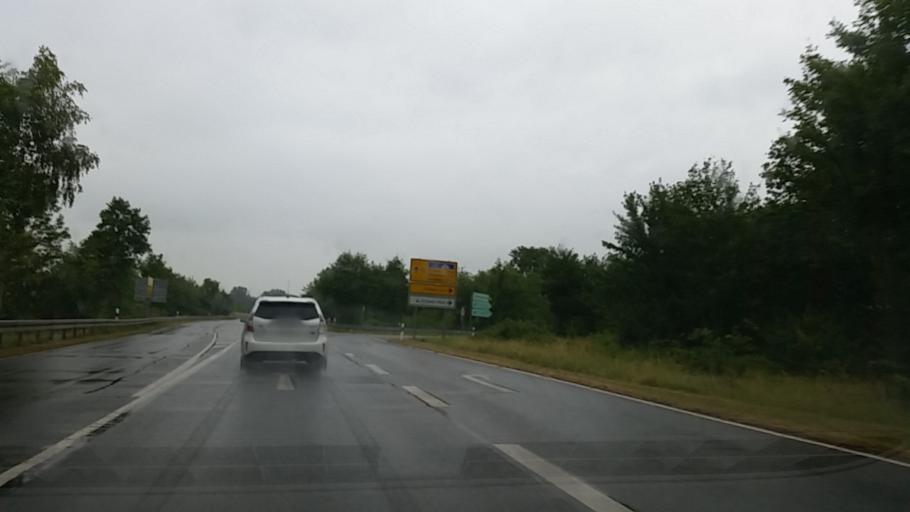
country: DE
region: Mecklenburg-Vorpommern
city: Kropelin
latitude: 54.0665
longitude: 11.7754
